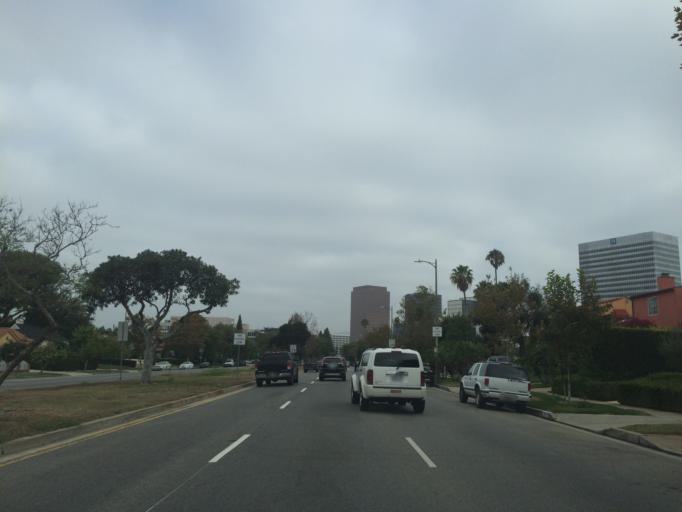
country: US
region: California
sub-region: Los Angeles County
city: West Hollywood
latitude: 34.0590
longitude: -118.3639
